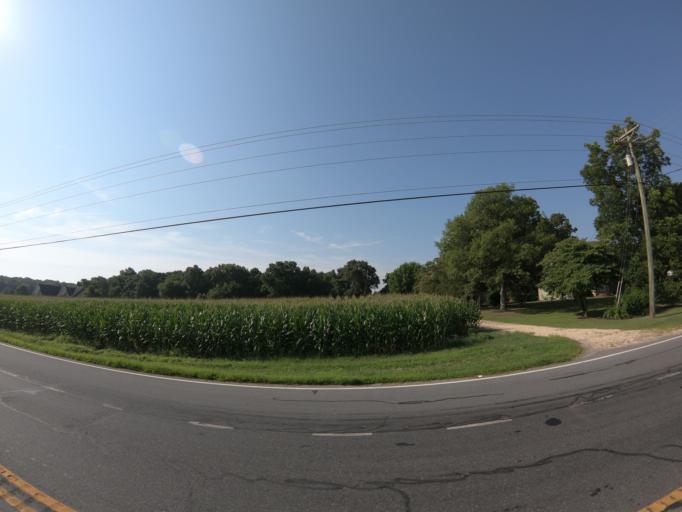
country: US
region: Delaware
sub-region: Sussex County
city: Bridgeville
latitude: 38.7081
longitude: -75.5513
